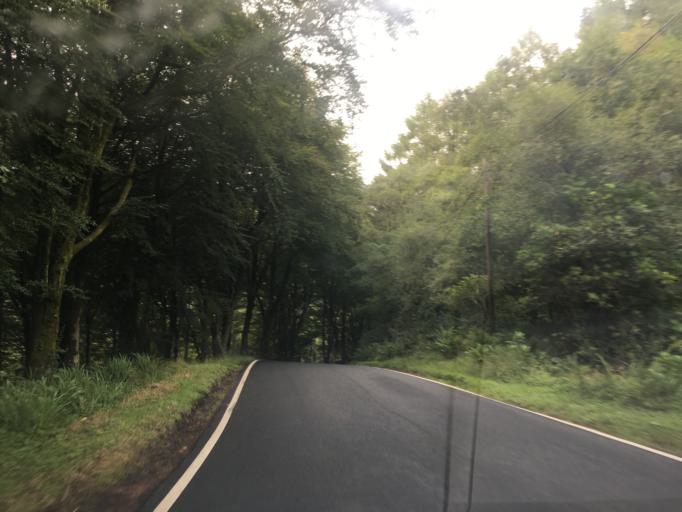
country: GB
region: Scotland
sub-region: Argyll and Bute
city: Port Bannatyne
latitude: 56.0010
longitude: -5.1164
